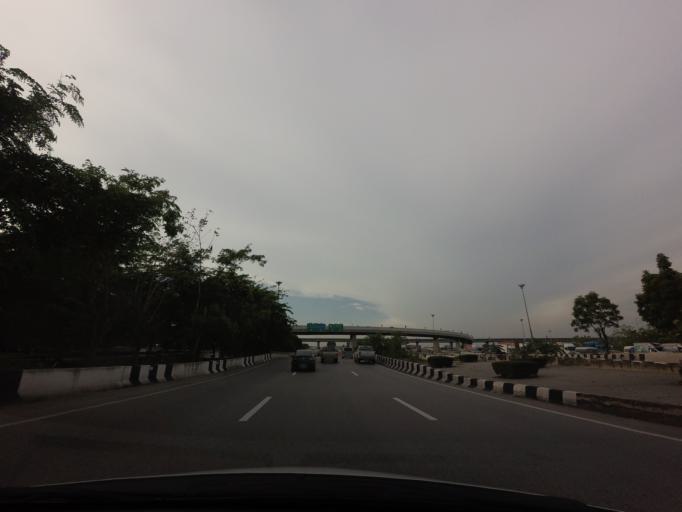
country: TH
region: Bangkok
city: Taling Chan
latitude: 13.7801
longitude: 100.4084
